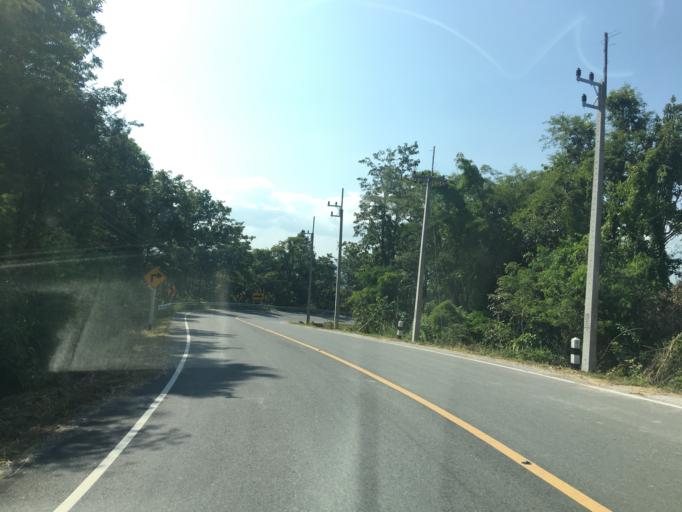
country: TH
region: Phayao
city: Chiang Muan
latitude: 18.8465
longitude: 100.3429
